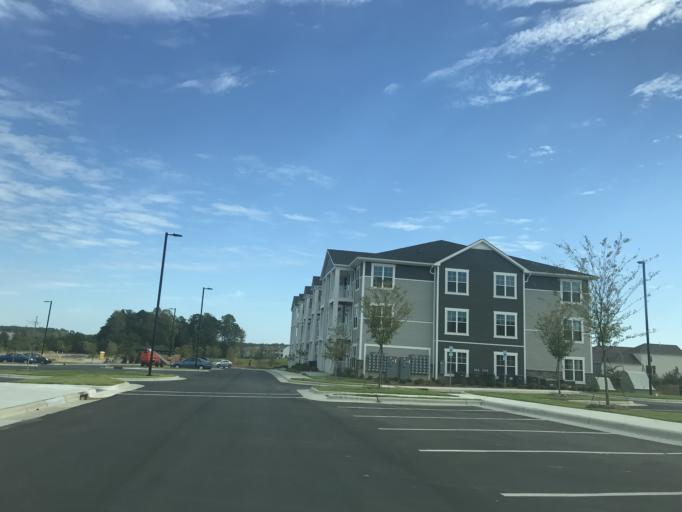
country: US
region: North Carolina
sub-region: Wake County
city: Knightdale
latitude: 35.8628
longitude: -78.5415
